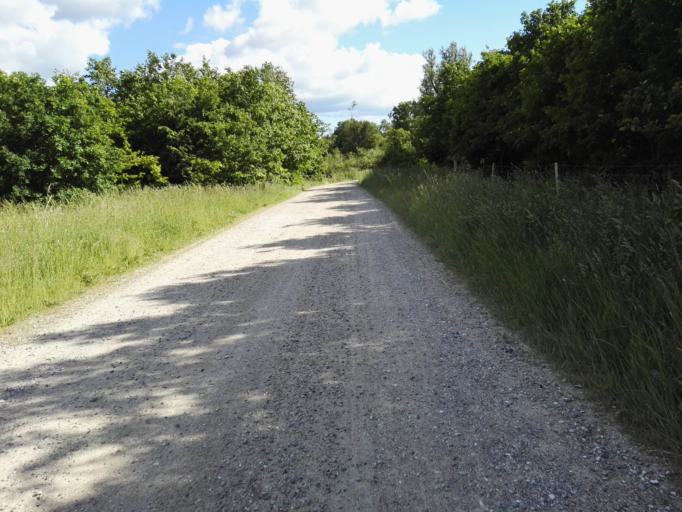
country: DK
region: Capital Region
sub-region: Egedal Kommune
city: Olstykke
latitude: 55.8016
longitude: 12.1686
